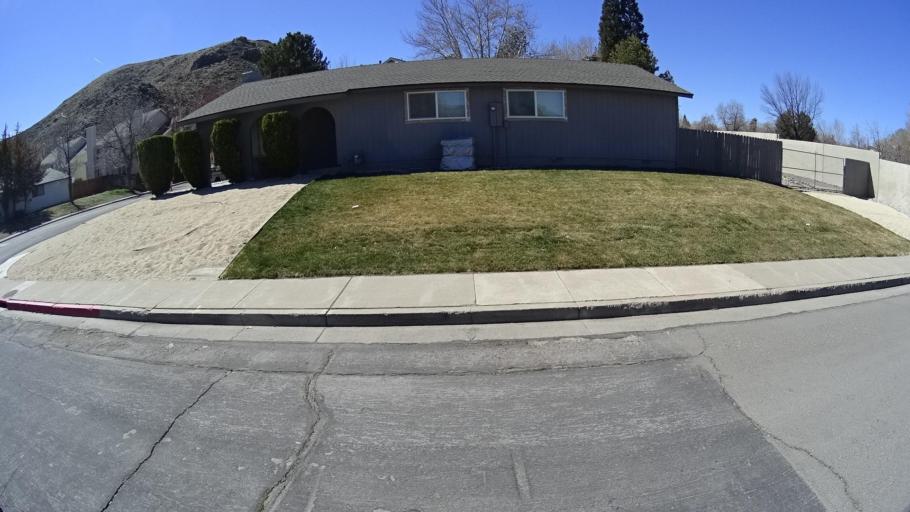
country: US
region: Nevada
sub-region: Washoe County
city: Sparks
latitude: 39.4785
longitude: -119.7547
